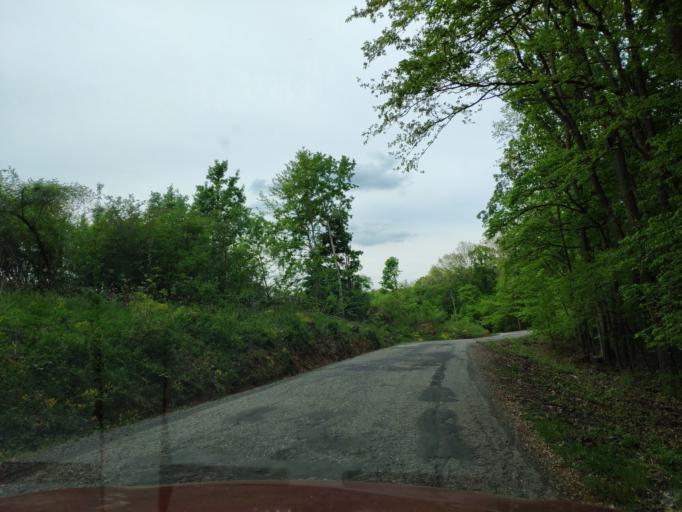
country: SK
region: Banskobystricky
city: Rimavska Sobota
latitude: 48.5156
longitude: 20.1058
